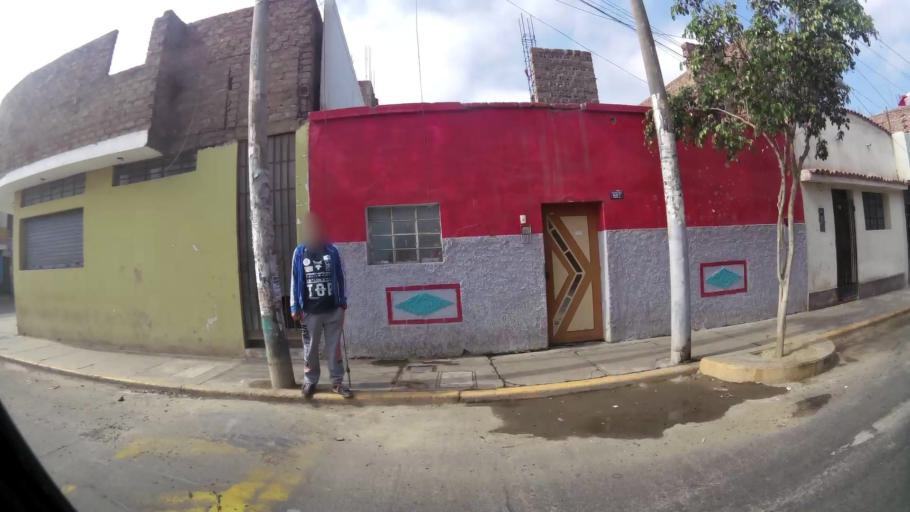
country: PE
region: La Libertad
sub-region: Provincia de Trujillo
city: Trujillo
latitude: -8.1151
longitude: -79.0186
